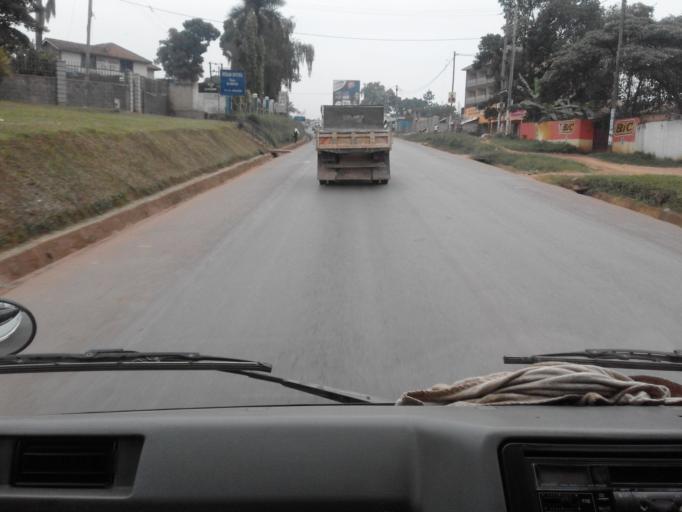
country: UG
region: Central Region
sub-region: Wakiso District
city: Bweyogerere
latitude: 0.3672
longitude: 32.7082
